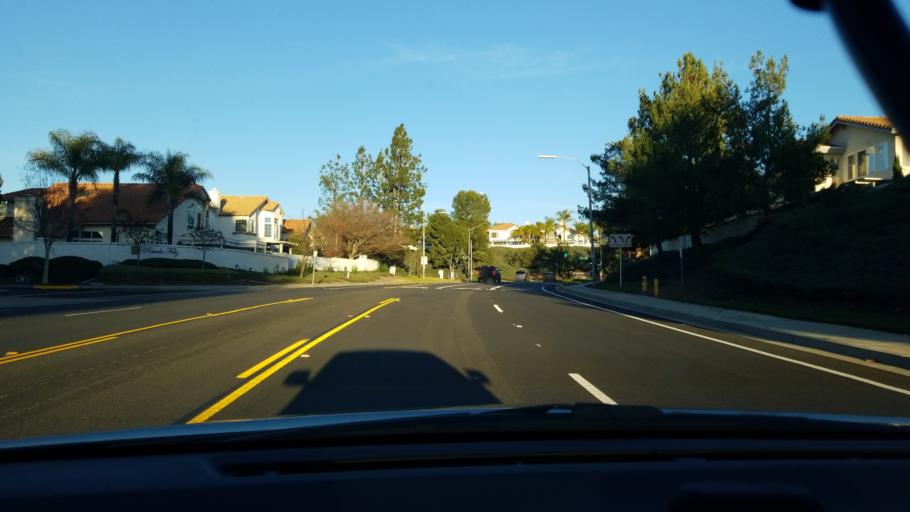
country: US
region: California
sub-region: Riverside County
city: Temecula
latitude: 33.4677
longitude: -117.0973
